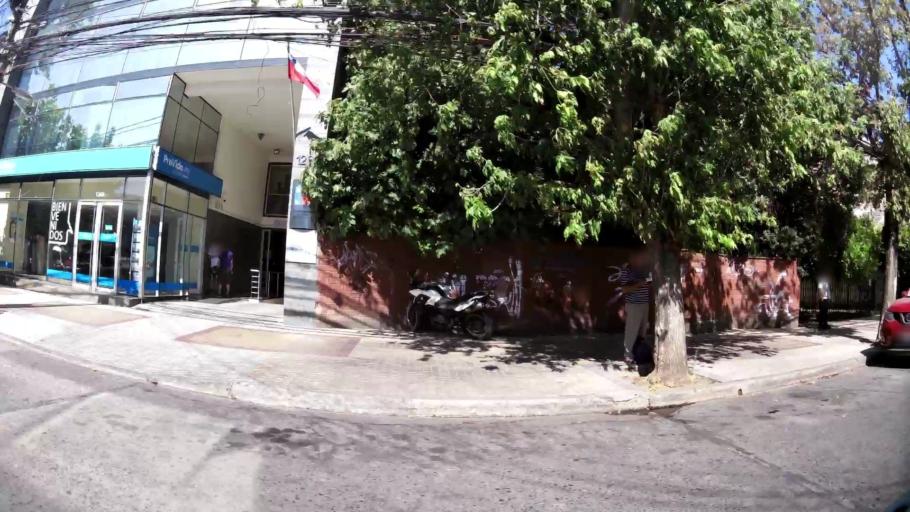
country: CL
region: Maule
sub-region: Provincia de Talca
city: Talca
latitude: -35.4252
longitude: -71.6637
